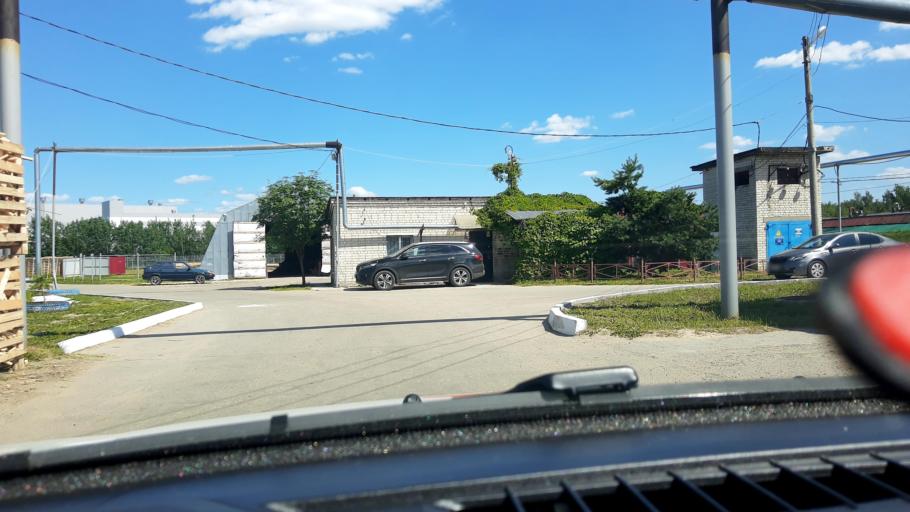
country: RU
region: Nizjnij Novgorod
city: Gorbatovka
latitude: 56.3024
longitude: 43.8073
